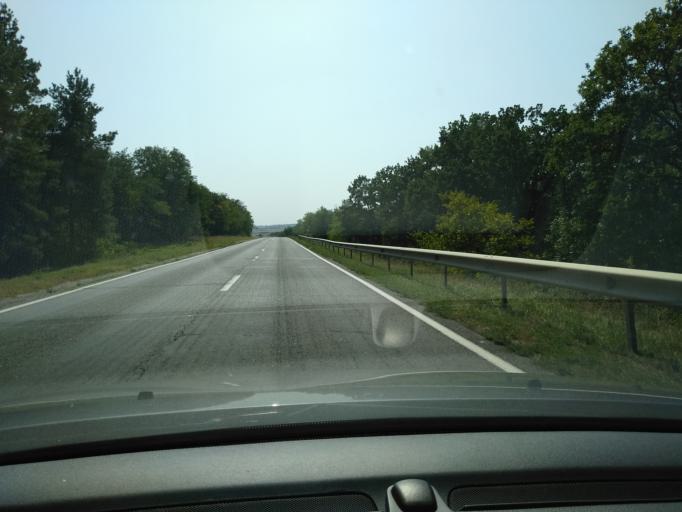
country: MD
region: Nisporeni
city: Nisporeni
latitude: 46.9963
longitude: 28.2742
